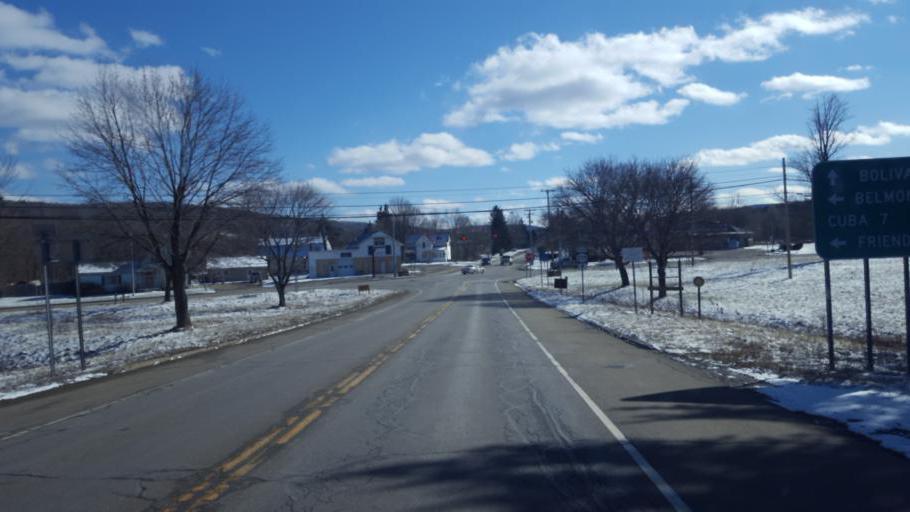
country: US
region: New York
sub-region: Allegany County
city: Friendship
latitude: 42.2039
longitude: -78.1453
